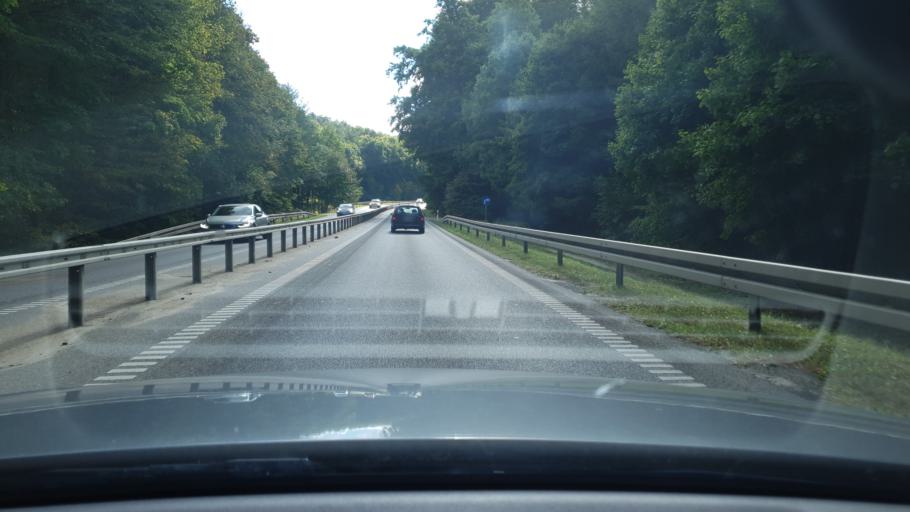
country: PL
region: Pomeranian Voivodeship
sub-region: Powiat wejherowski
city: Reda
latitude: 54.6257
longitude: 18.3413
